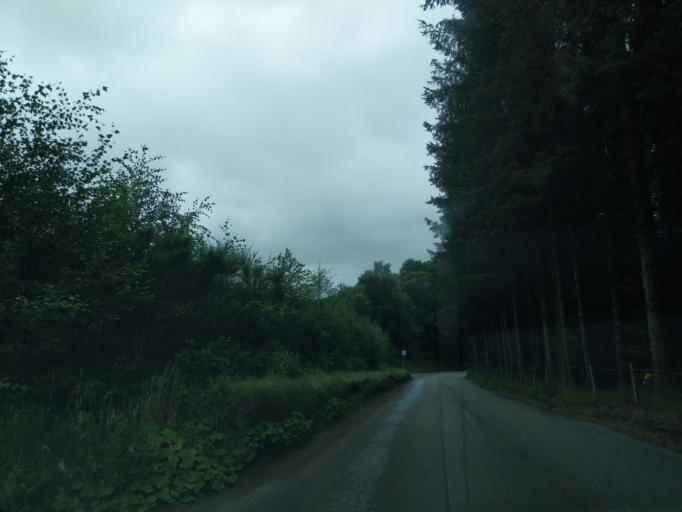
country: GB
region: Scotland
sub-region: Moray
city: Rothes
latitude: 57.4789
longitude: -3.1858
